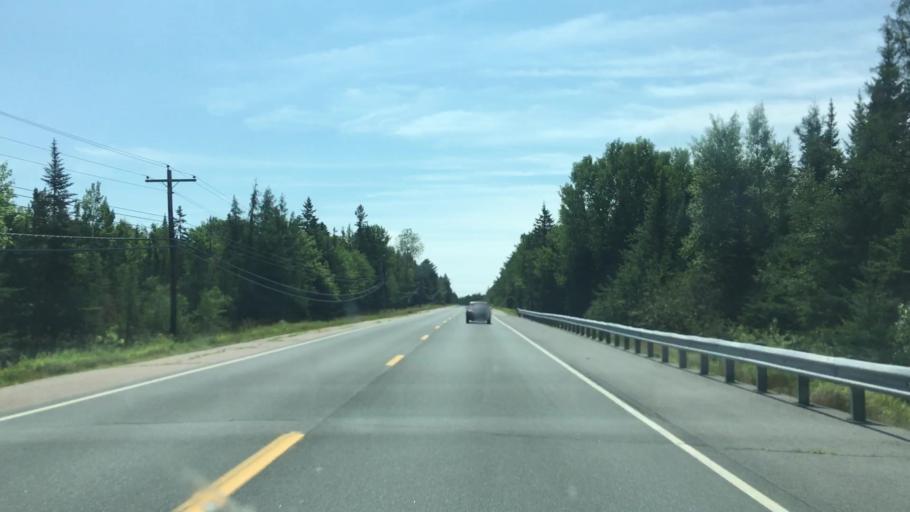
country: US
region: Maine
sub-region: Washington County
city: Calais
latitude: 45.1465
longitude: -67.1683
